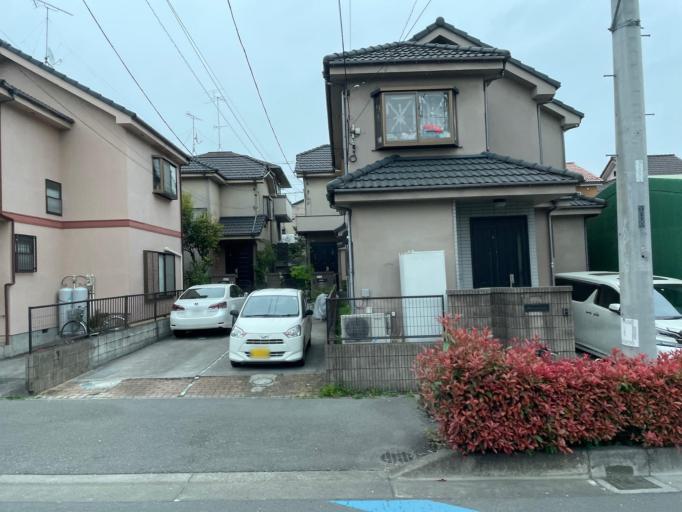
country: JP
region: Saitama
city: Saitama
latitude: 35.8877
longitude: 139.6915
